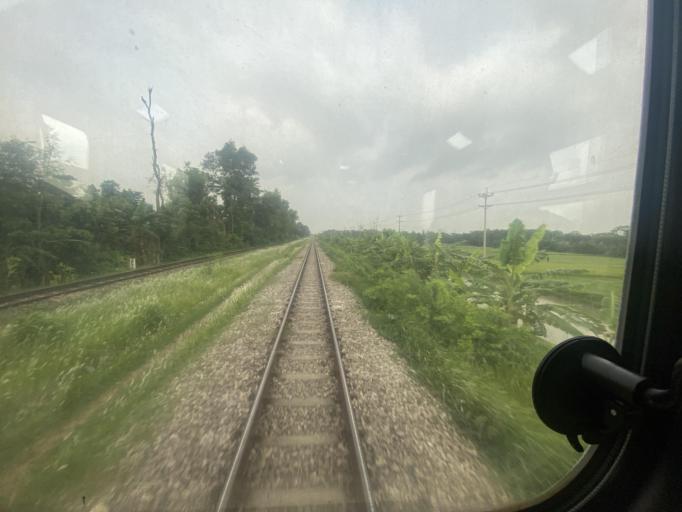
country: BD
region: Dhaka
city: Tungi
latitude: 23.9326
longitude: 90.5168
